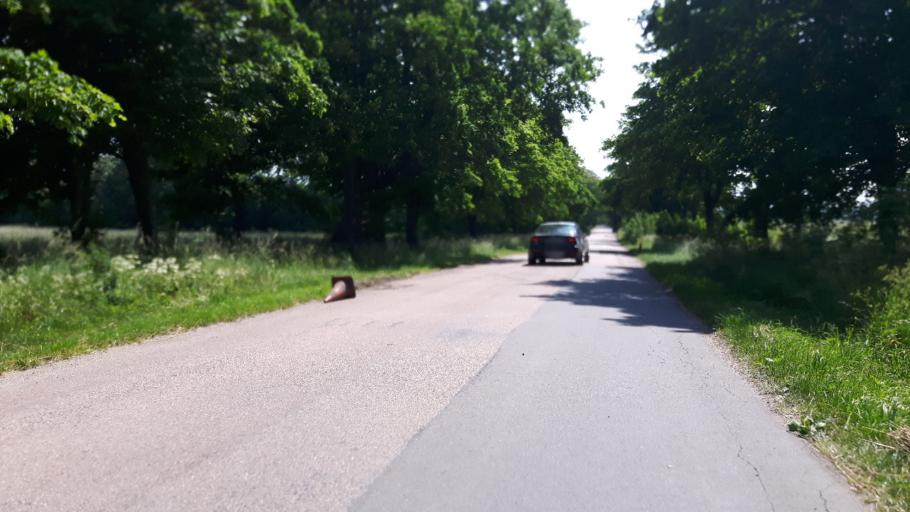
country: PL
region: Pomeranian Voivodeship
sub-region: Powiat wejherowski
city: Choczewo
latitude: 54.7448
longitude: 17.8089
